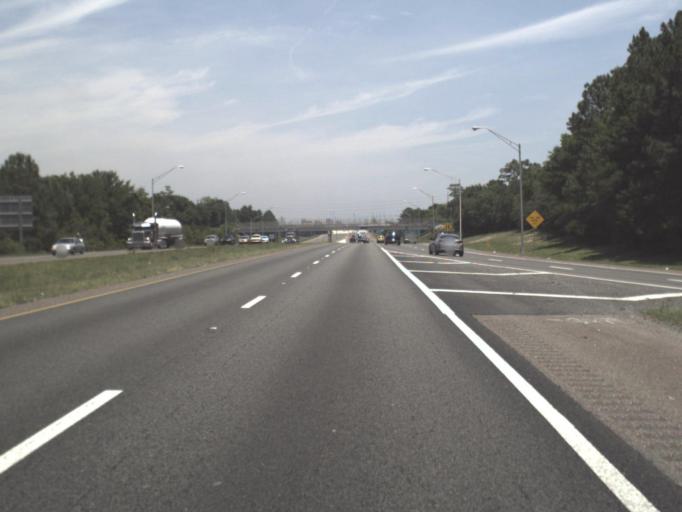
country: US
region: Florida
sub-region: Duval County
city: Jacksonville
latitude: 30.3586
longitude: -81.5542
